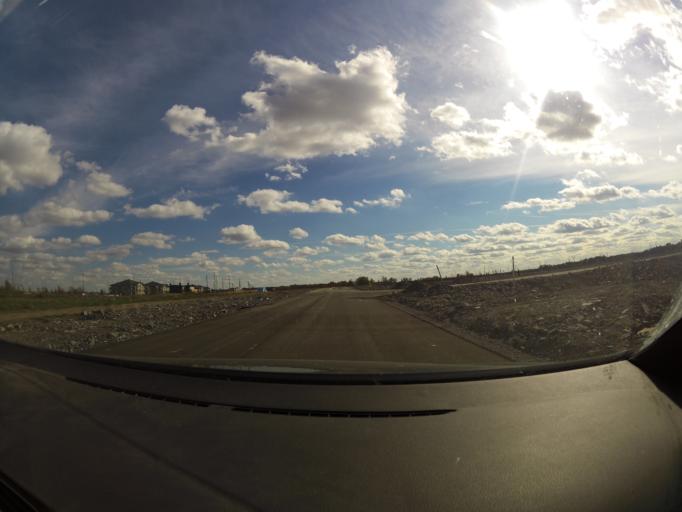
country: CA
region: Ontario
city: Bells Corners
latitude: 45.2715
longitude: -75.8948
